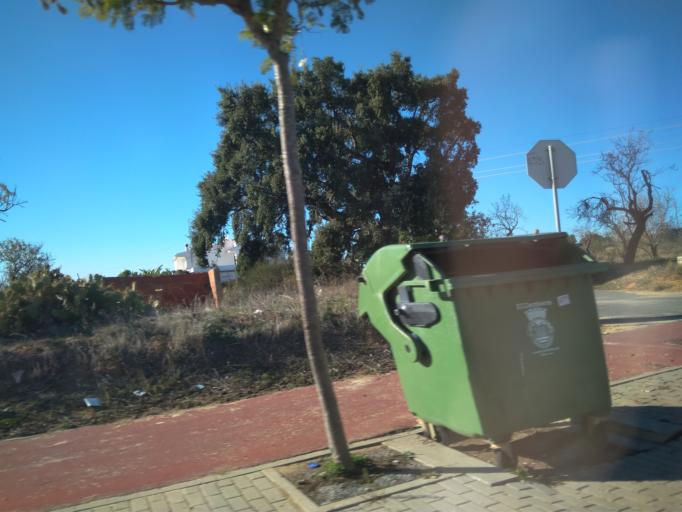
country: PT
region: Faro
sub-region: Albufeira
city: Ferreiras
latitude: 37.1115
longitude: -8.2284
